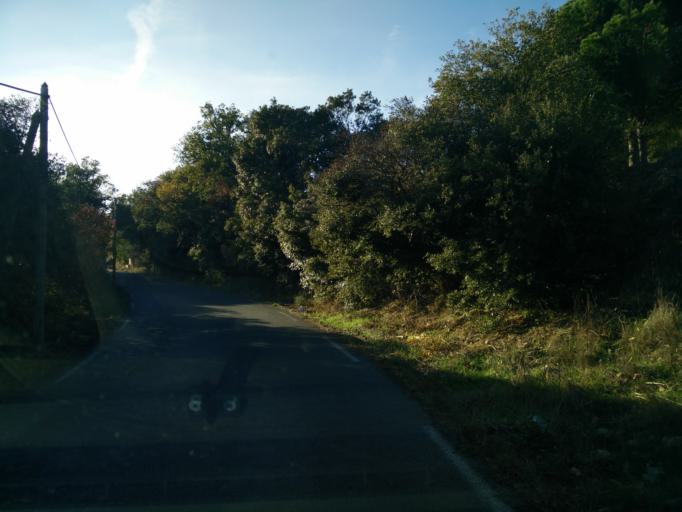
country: FR
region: Provence-Alpes-Cote d'Azur
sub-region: Departement du Var
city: Le Plan-de-la-Tour
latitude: 43.3376
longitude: 6.5413
